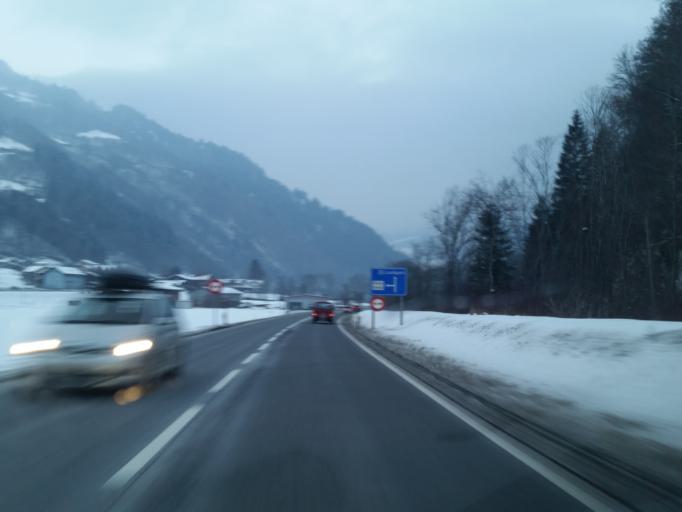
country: CH
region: Grisons
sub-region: Praettigau/Davos District
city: Jenaz
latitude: 46.9357
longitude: 9.7123
